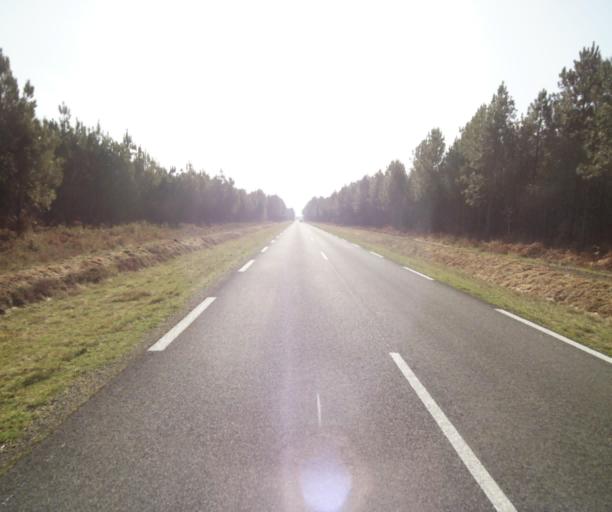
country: FR
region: Aquitaine
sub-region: Departement de la Gironde
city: Grignols
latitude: 44.1838
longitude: -0.1450
